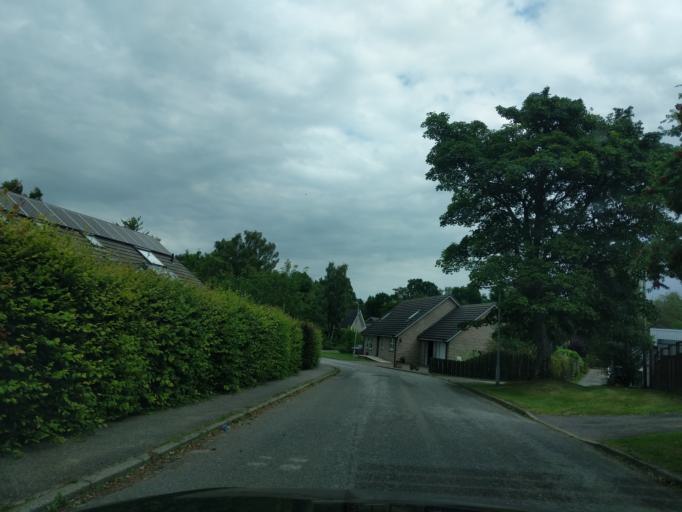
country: GB
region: Scotland
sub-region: Aberdeenshire
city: Aboyne
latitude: 57.0800
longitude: -2.7728
